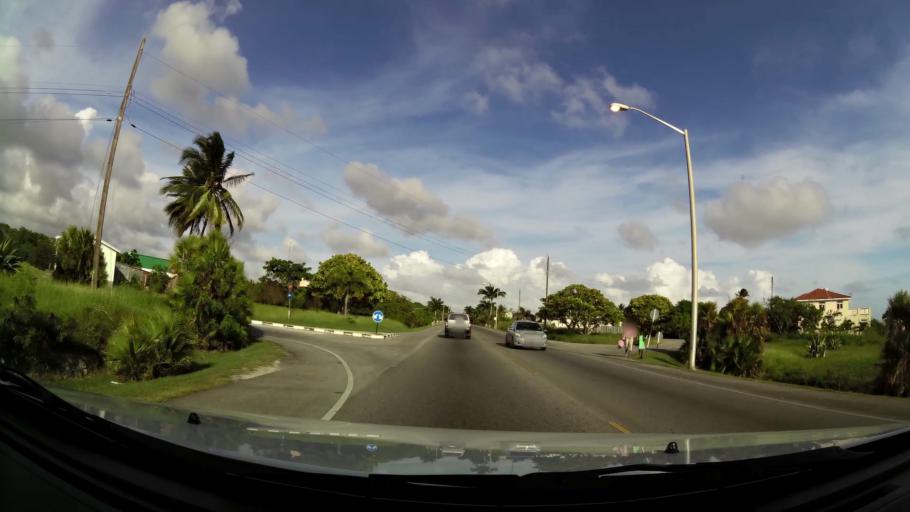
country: BB
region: Christ Church
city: Oistins
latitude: 13.0771
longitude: -59.5632
